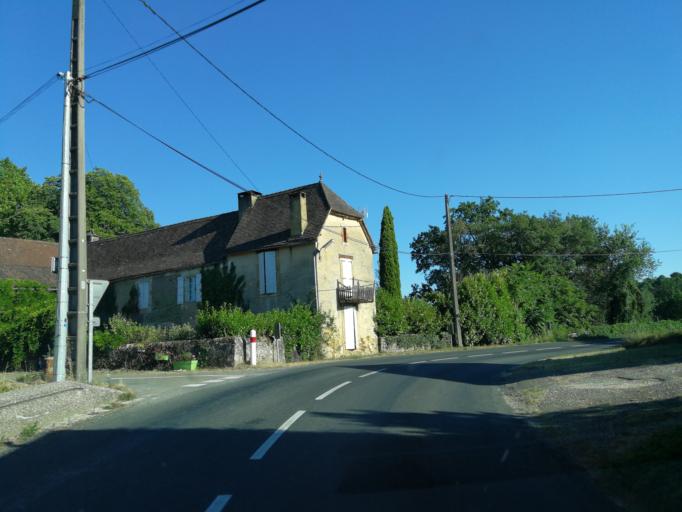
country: FR
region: Midi-Pyrenees
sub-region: Departement du Lot
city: Salviac
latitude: 44.6142
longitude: 1.2100
